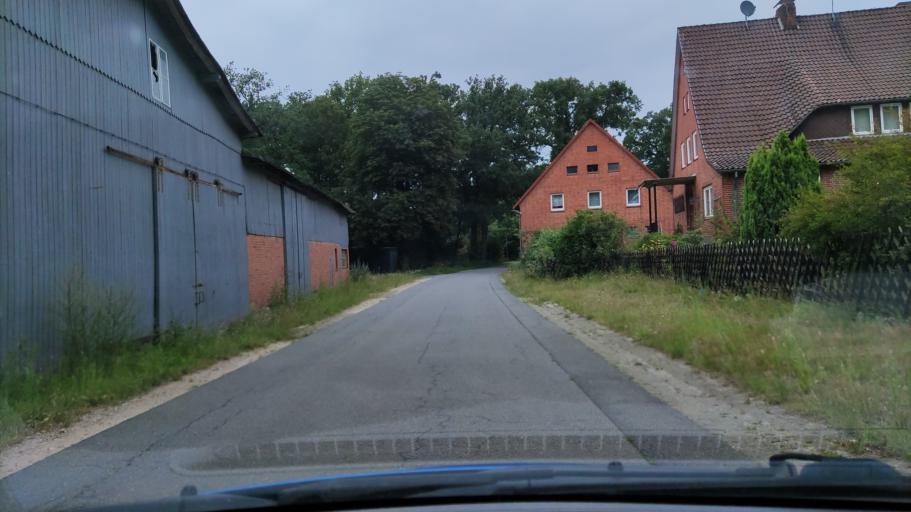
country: DE
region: Lower Saxony
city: Stoetze
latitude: 53.0325
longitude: 10.7633
